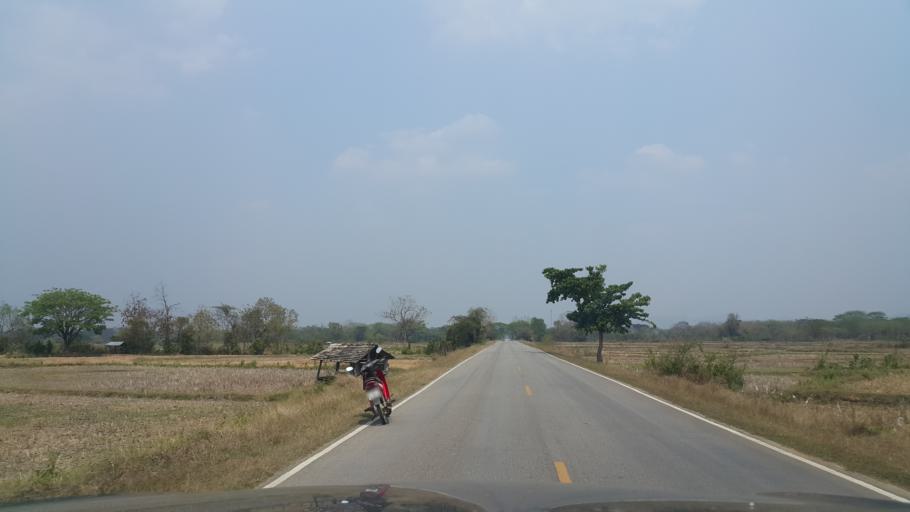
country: TH
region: Lampang
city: Soem Ngam
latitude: 17.9975
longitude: 99.1793
